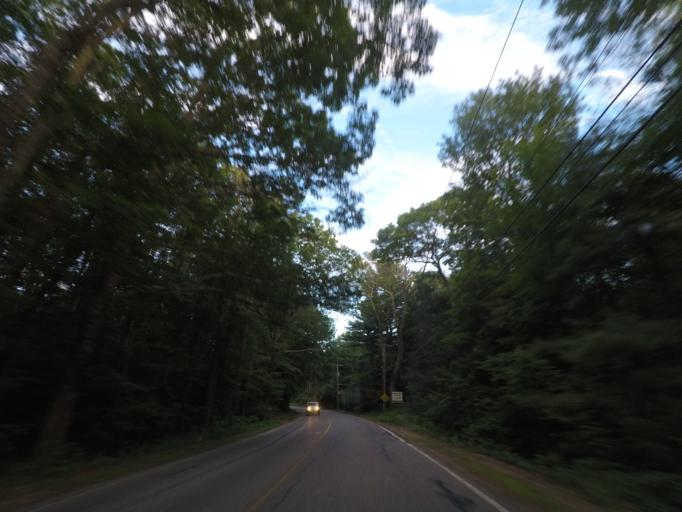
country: US
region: Massachusetts
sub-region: Worcester County
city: Warren
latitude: 42.1935
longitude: -72.1808
